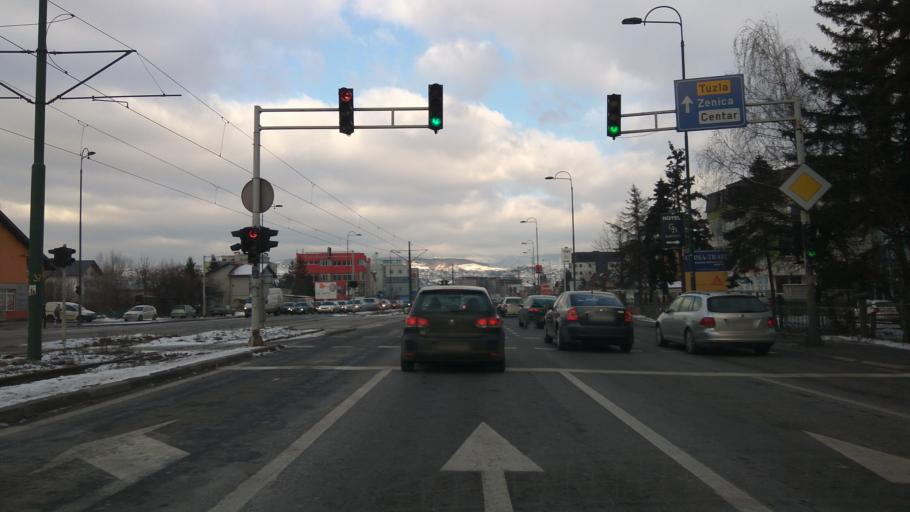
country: BA
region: Federation of Bosnia and Herzegovina
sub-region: Kanton Sarajevo
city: Sarajevo
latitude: 43.8372
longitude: 18.3172
